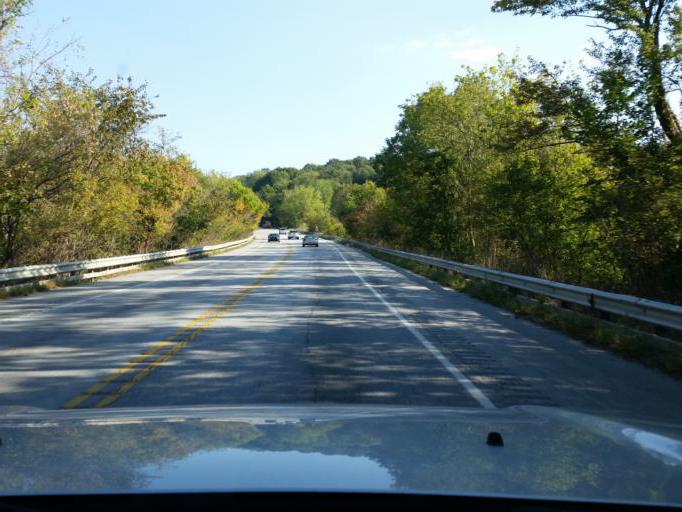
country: US
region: Pennsylvania
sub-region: Chester County
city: Atglen
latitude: 39.9435
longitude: -75.9665
